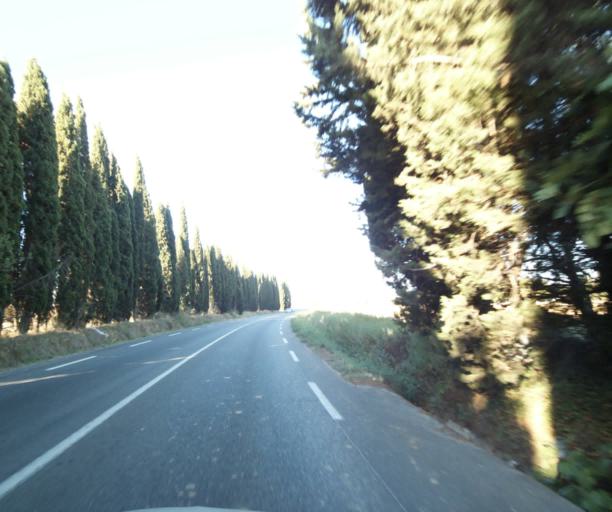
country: FR
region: Languedoc-Roussillon
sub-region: Departement du Gard
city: Bouillargues
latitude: 43.8059
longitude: 4.4108
